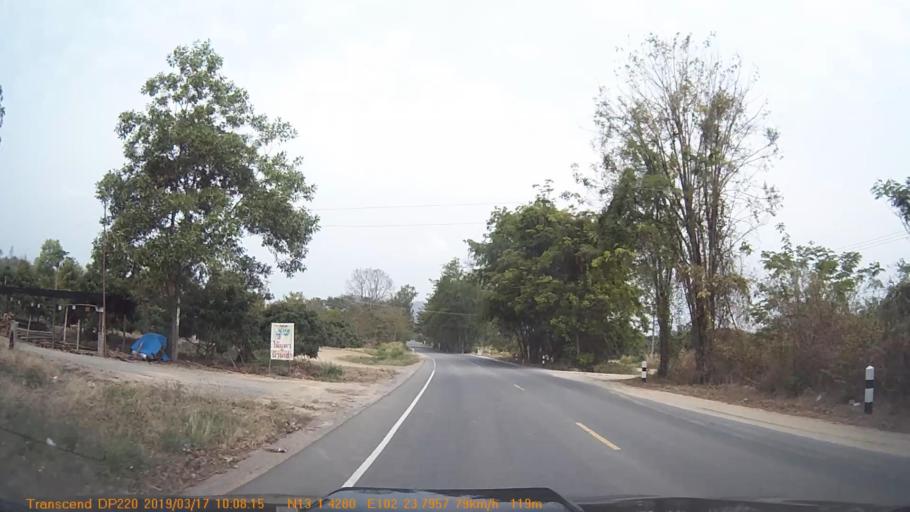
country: TH
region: Chanthaburi
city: Pong Nam Ron
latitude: 13.0257
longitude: 102.3955
